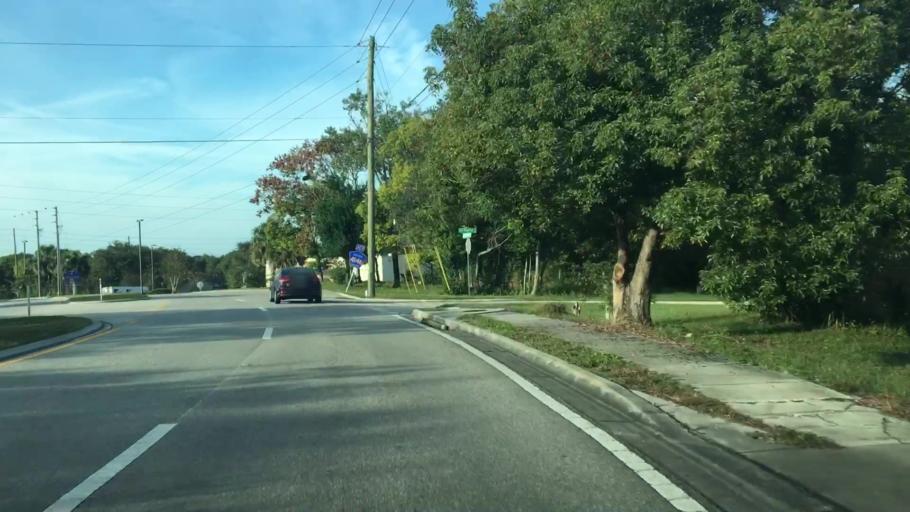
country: US
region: Florida
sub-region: Volusia County
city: Deltona
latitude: 28.9116
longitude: -81.2587
